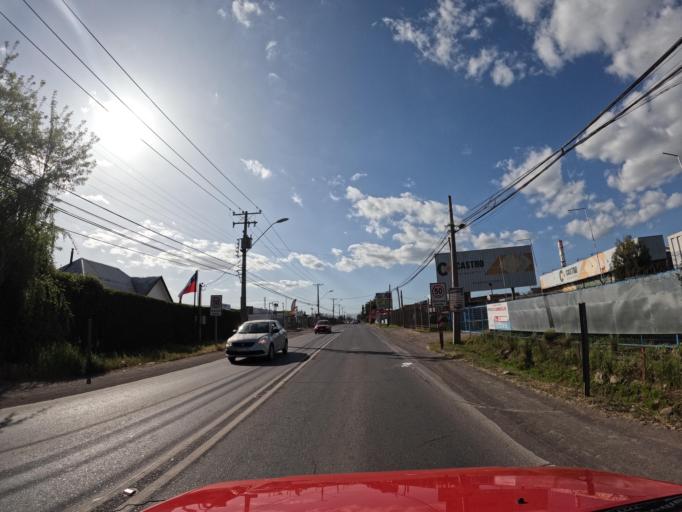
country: CL
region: Maule
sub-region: Provincia de Curico
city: Curico
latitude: -34.9630
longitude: -71.2496
